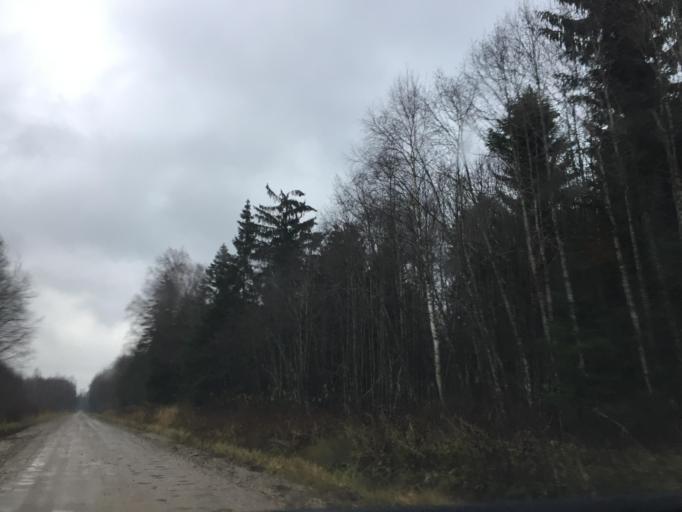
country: LV
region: Aloja
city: Staicele
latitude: 57.7521
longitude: 24.6001
